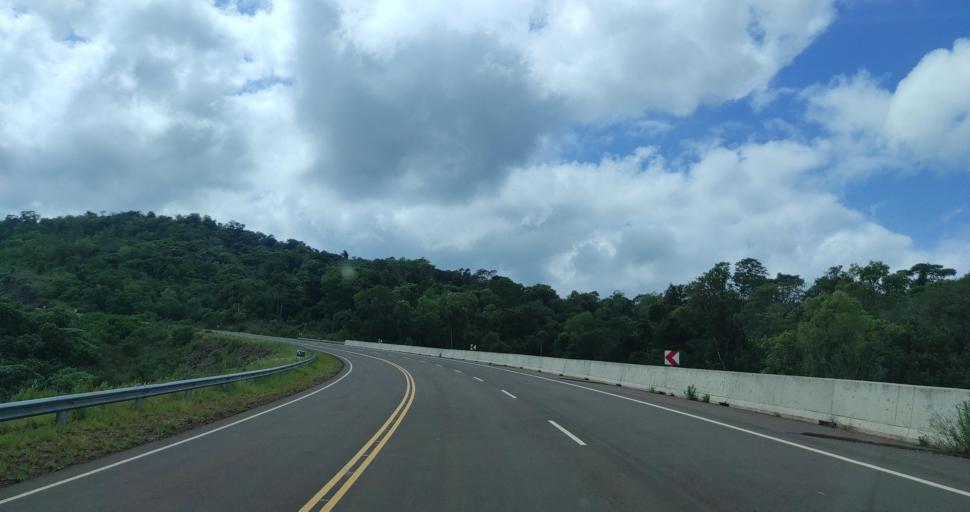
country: AR
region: Misiones
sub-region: Departamento de Veinticinco de Mayo
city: Veinticinco de Mayo
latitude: -27.3837
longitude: -54.8175
